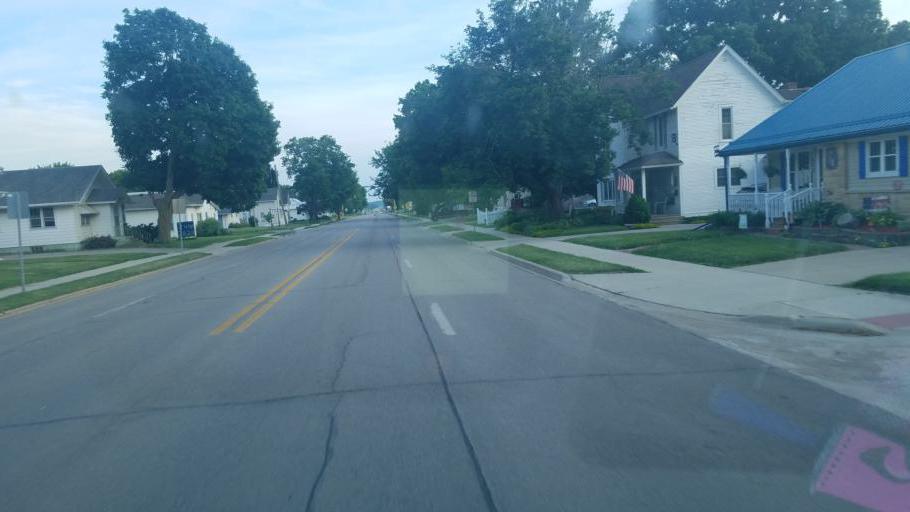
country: US
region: Iowa
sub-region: Benton County
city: Belle Plaine
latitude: 41.8931
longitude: -92.2782
